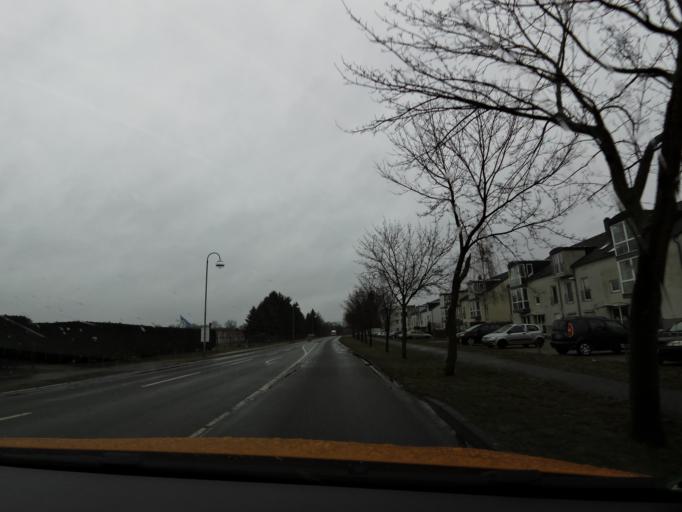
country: DE
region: Brandenburg
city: Zossen
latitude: 52.2031
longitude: 13.4319
